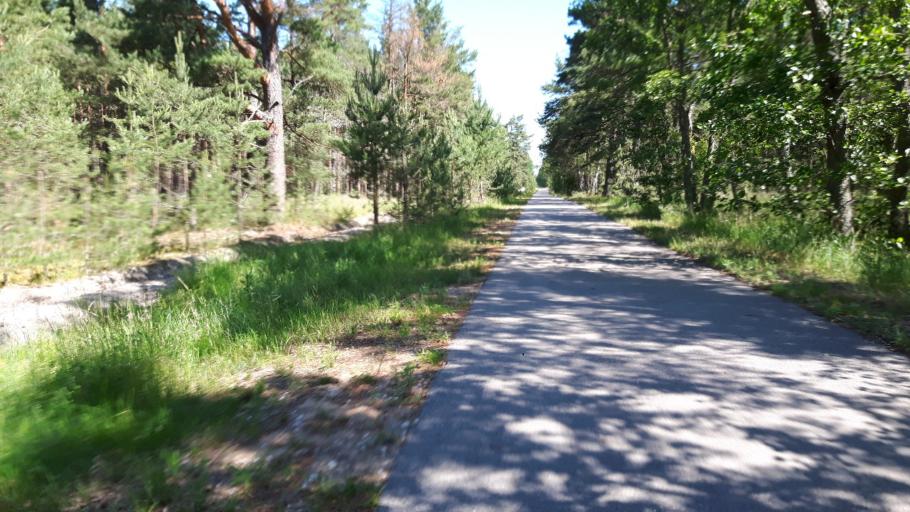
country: LT
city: Nida
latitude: 55.3361
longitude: 21.0358
